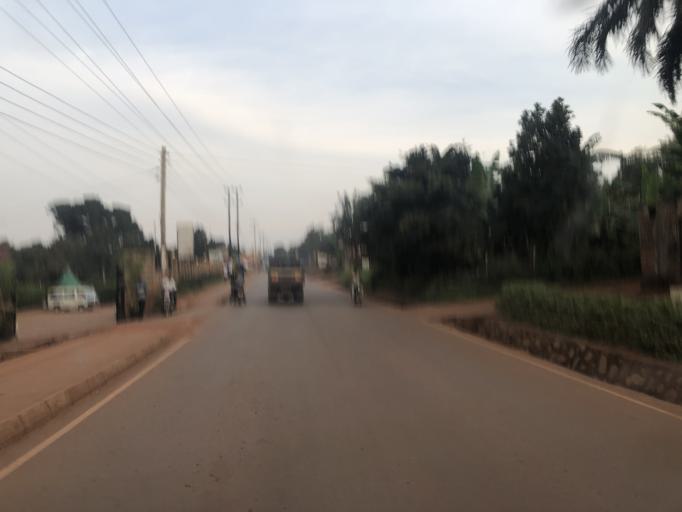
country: UG
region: Central Region
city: Kampala Central Division
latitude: 0.2880
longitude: 32.5371
